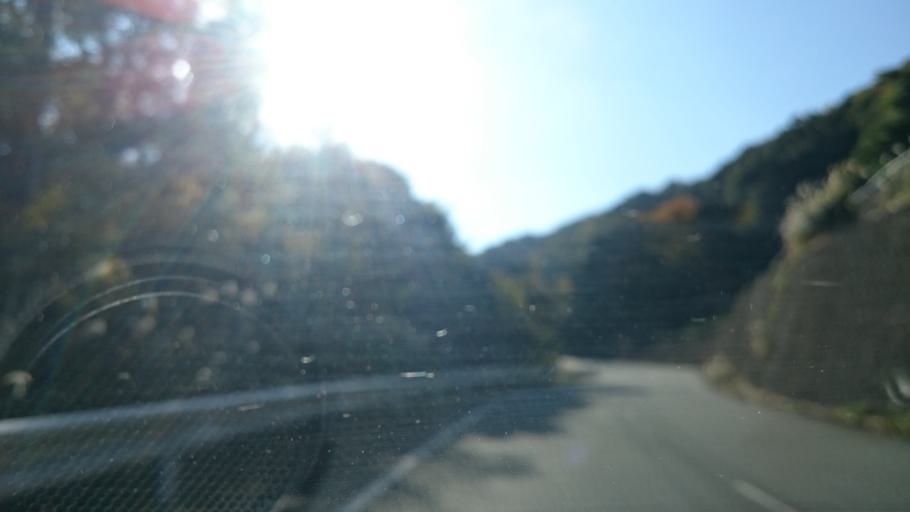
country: JP
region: Shizuoka
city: Heda
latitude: 35.0071
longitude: 138.8321
